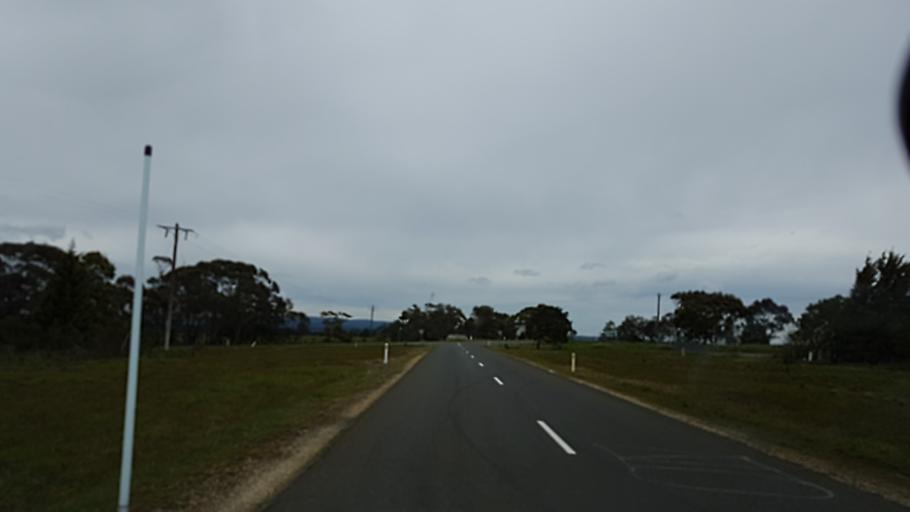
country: AU
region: Victoria
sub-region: Moorabool
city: Bacchus Marsh
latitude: -37.6251
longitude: 144.2097
